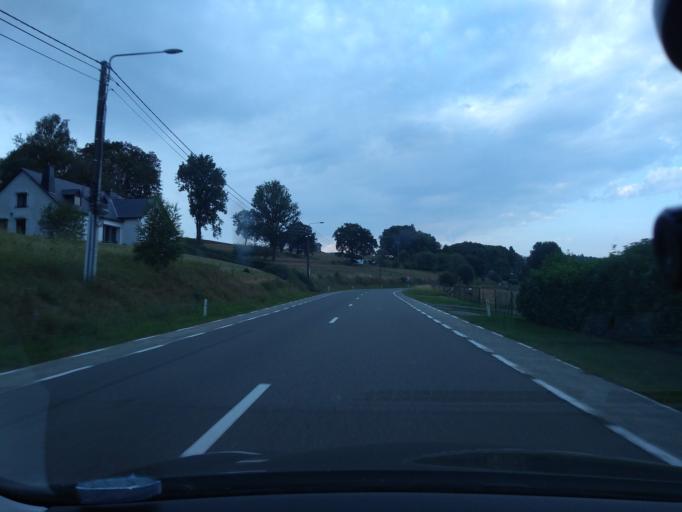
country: BE
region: Wallonia
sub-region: Province du Luxembourg
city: Saint-Hubert
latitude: 50.0235
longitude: 5.3513
